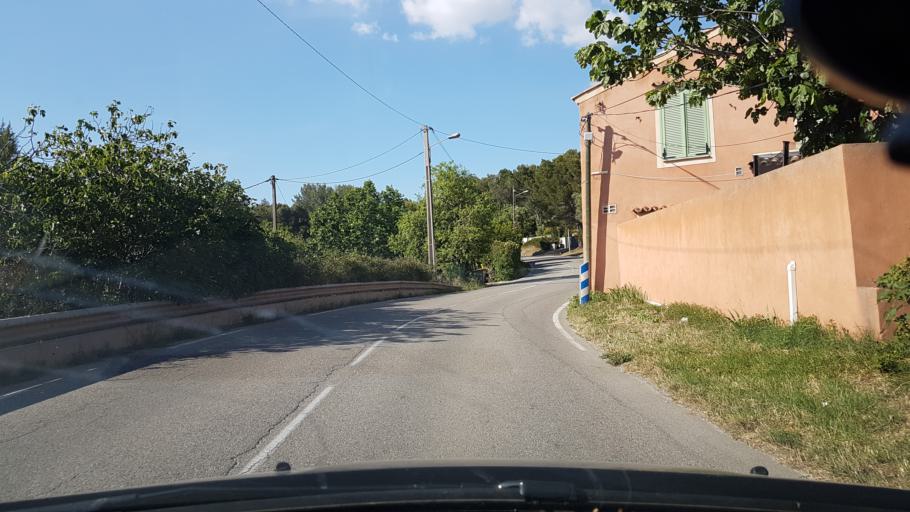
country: FR
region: Provence-Alpes-Cote d'Azur
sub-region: Departement des Bouches-du-Rhone
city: Carnoux-en-Provence
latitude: 43.2402
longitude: 5.5623
